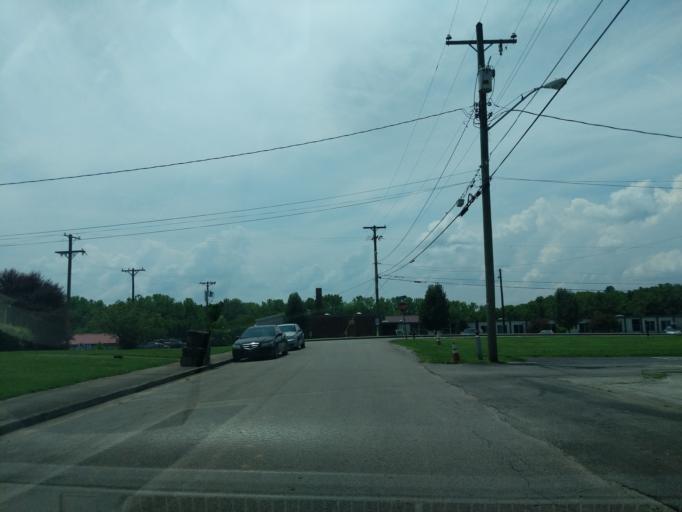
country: US
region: Tennessee
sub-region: Davidson County
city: Lakewood
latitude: 36.2271
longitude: -86.6328
